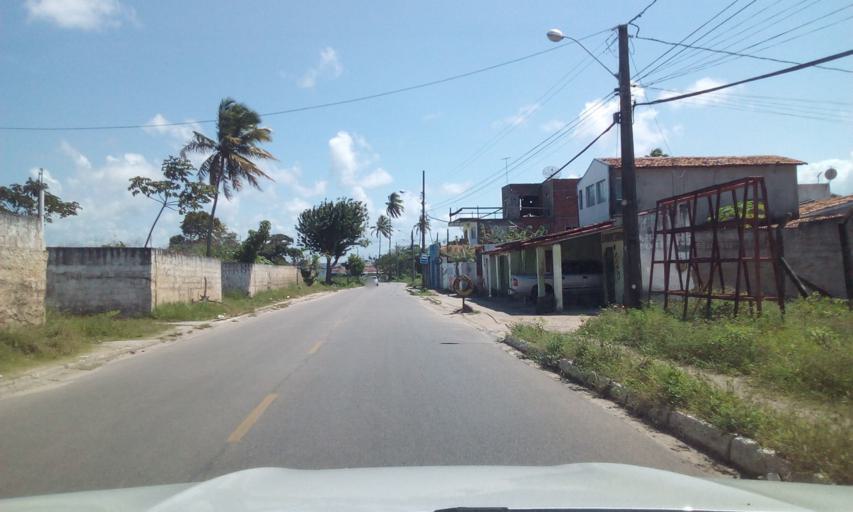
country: BR
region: Paraiba
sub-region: Conde
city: Conde
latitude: -7.2068
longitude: -34.8323
